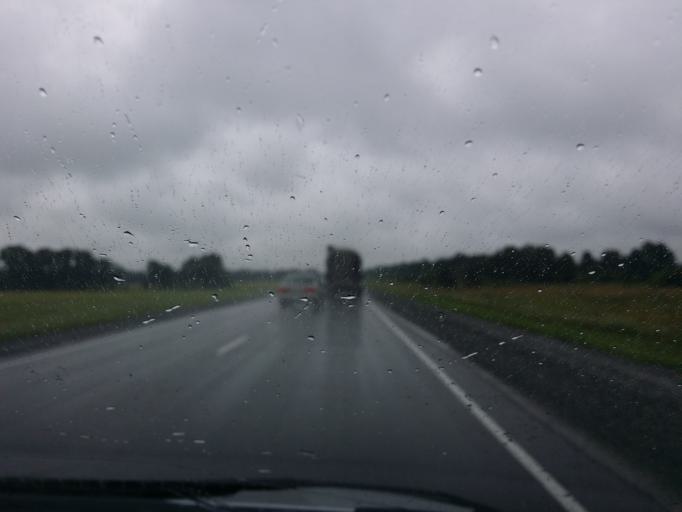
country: RU
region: Altai Krai
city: Bayunovskiye Klyuchi
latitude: 53.3116
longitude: 84.2317
